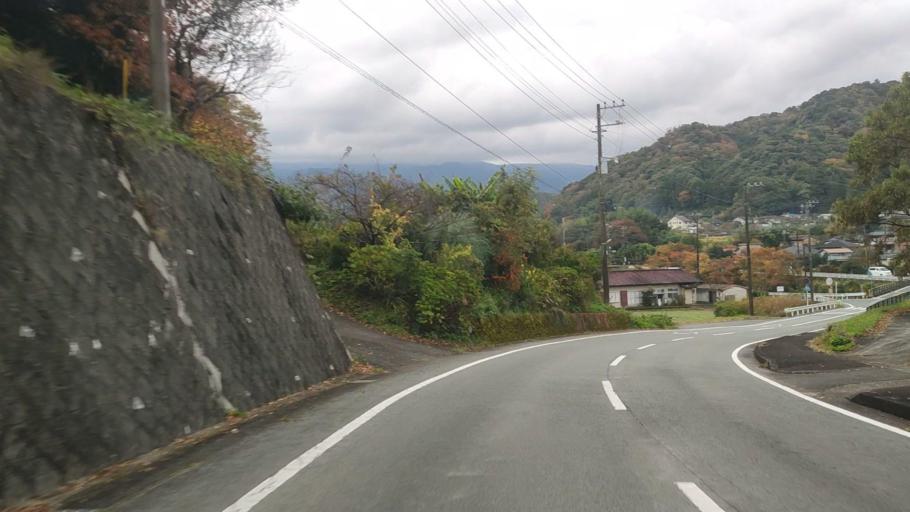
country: JP
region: Shizuoka
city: Ito
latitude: 34.9470
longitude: 138.9977
